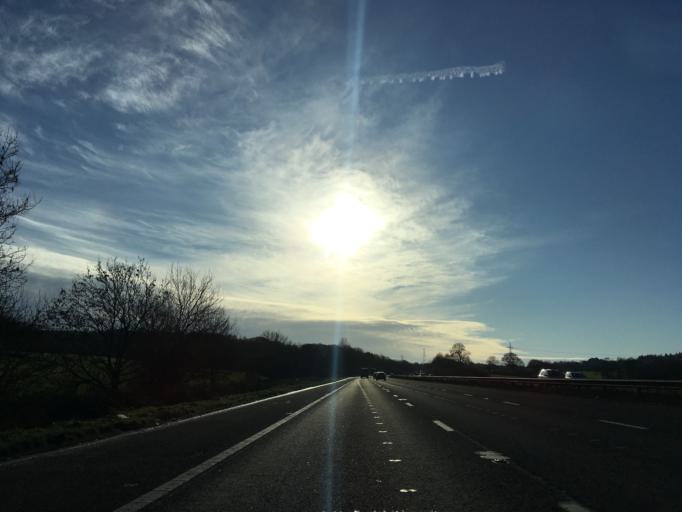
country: GB
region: England
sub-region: South Gloucestershire
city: Falfield
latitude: 51.6182
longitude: -2.4631
